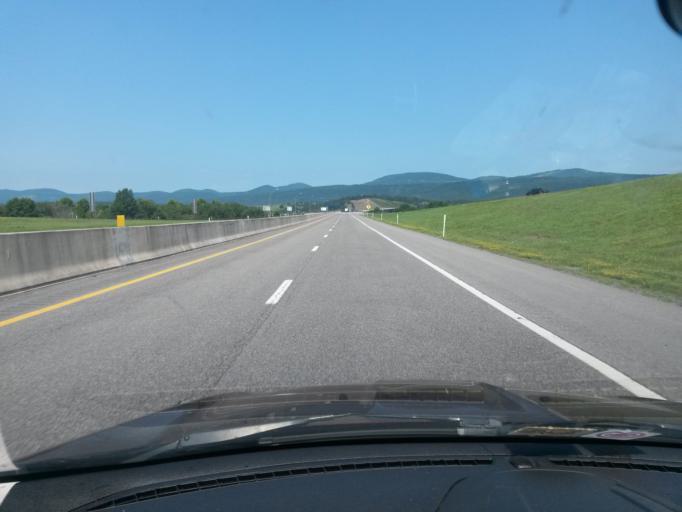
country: US
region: West Virginia
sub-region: Hardy County
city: Moorefield
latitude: 39.0786
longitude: -78.9528
